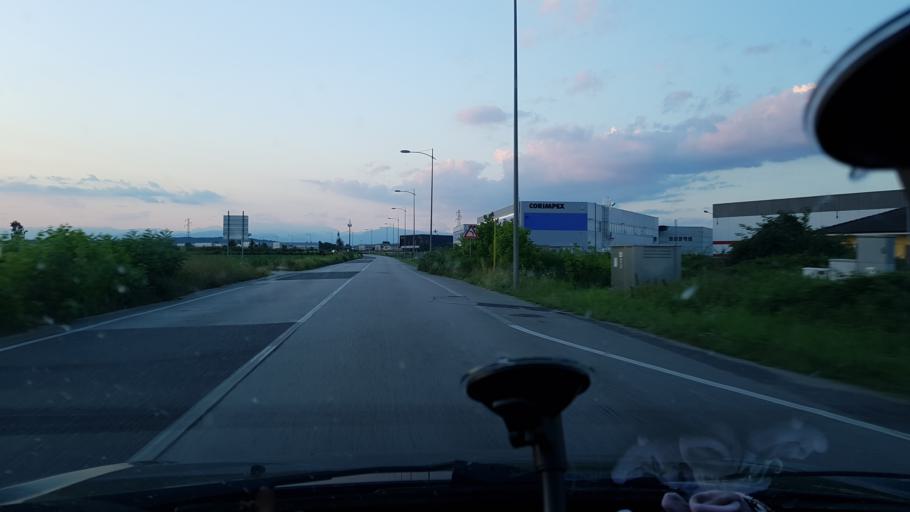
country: IT
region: Friuli Venezia Giulia
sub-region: Provincia di Gorizia
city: Villesse
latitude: 45.8755
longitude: 13.4360
